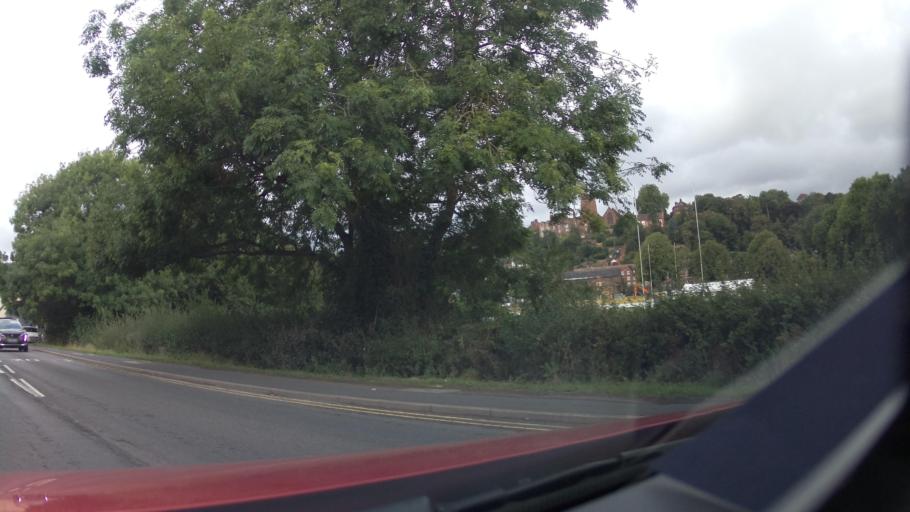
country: GB
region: England
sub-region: Shropshire
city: Bridgnorth
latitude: 52.5367
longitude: -2.4114
